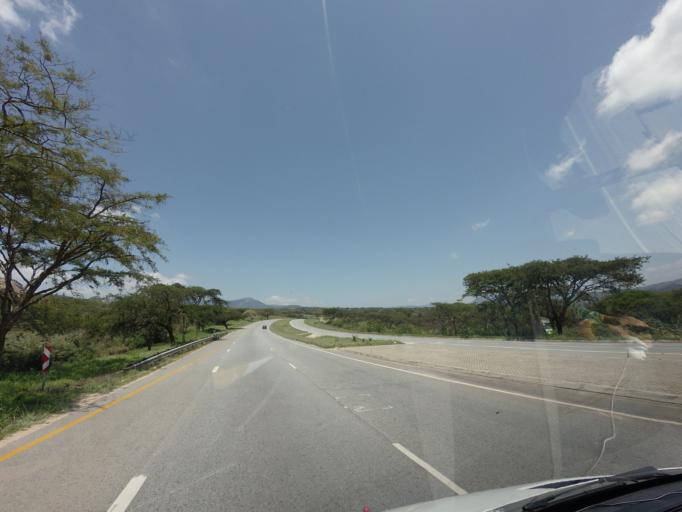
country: ZA
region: Mpumalanga
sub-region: Ehlanzeni District
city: Nelspruit
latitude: -25.4466
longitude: 30.8680
